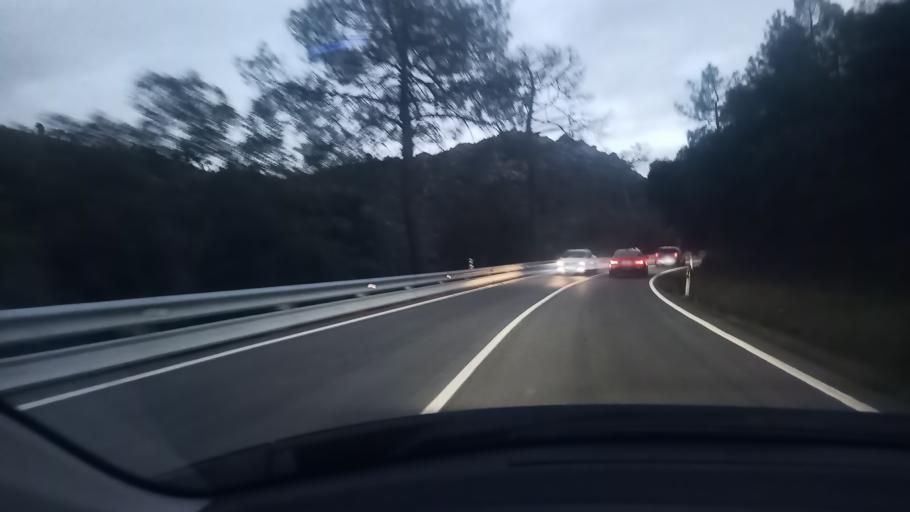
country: ES
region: Madrid
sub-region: Provincia de Madrid
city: Robledo de Chavela
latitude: 40.4621
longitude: -4.2629
